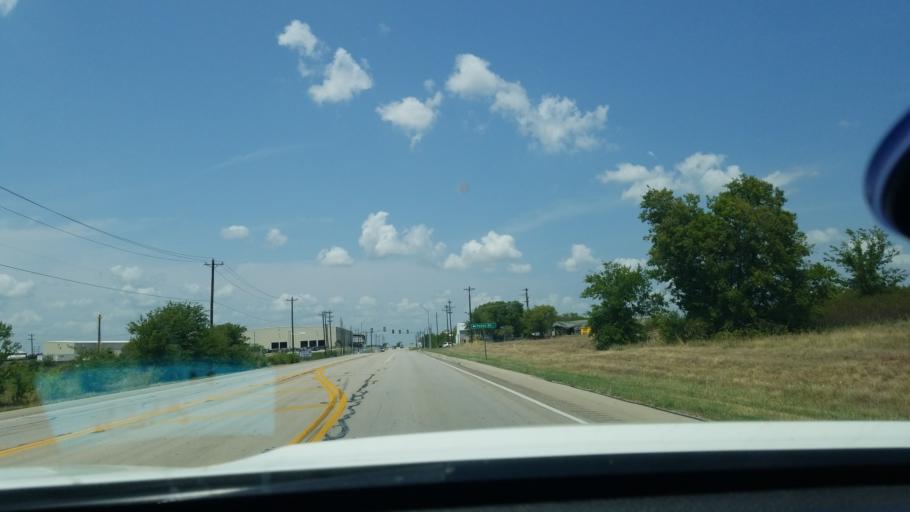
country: US
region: Texas
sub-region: Tarrant County
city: Eagle Mountain
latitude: 32.9332
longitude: -97.4166
